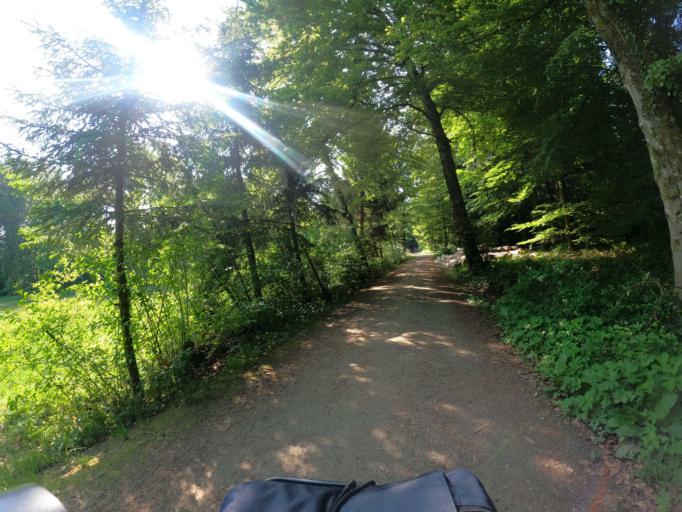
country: CH
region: Zug
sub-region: Zug
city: Steinhausen
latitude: 47.2137
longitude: 8.4969
